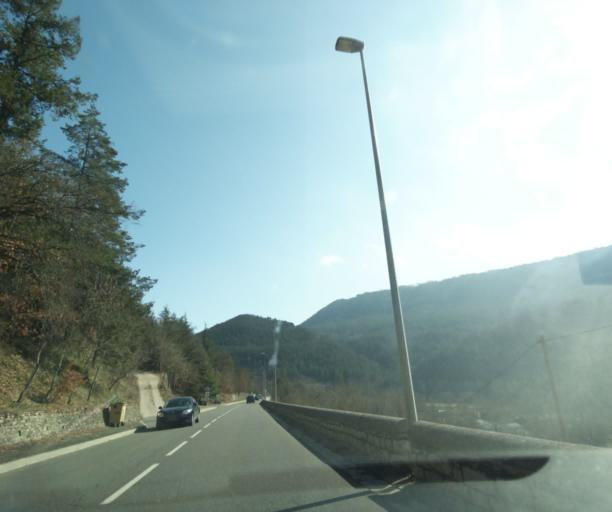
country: FR
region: Languedoc-Roussillon
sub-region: Departement de la Lozere
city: Mende
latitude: 44.5349
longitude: 3.5551
